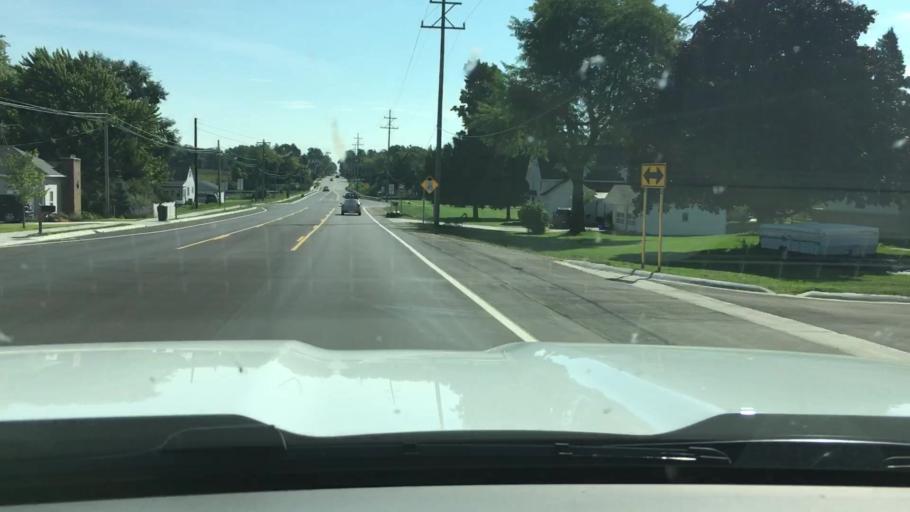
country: US
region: Michigan
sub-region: Gratiot County
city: Saint Louis
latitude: 43.4079
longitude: -84.6229
